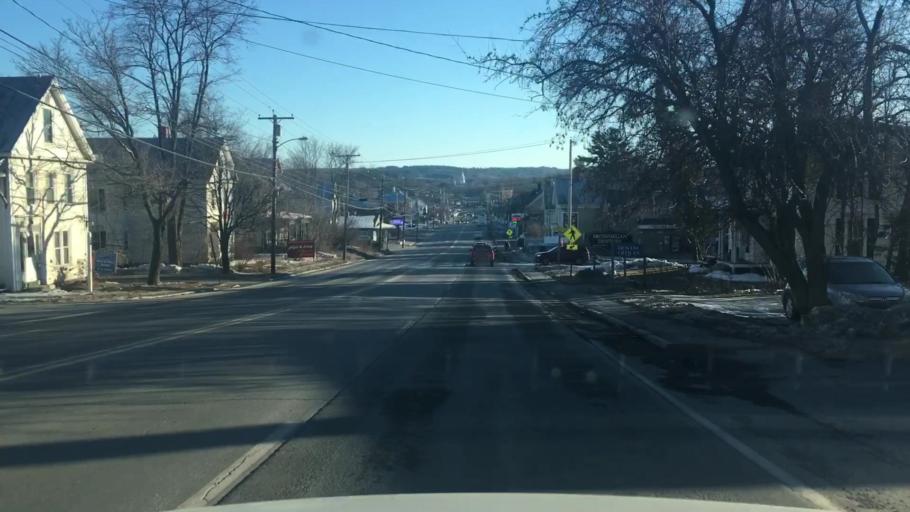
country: US
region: Maine
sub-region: Somerset County
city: Skowhegan
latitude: 44.7712
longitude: -69.7222
